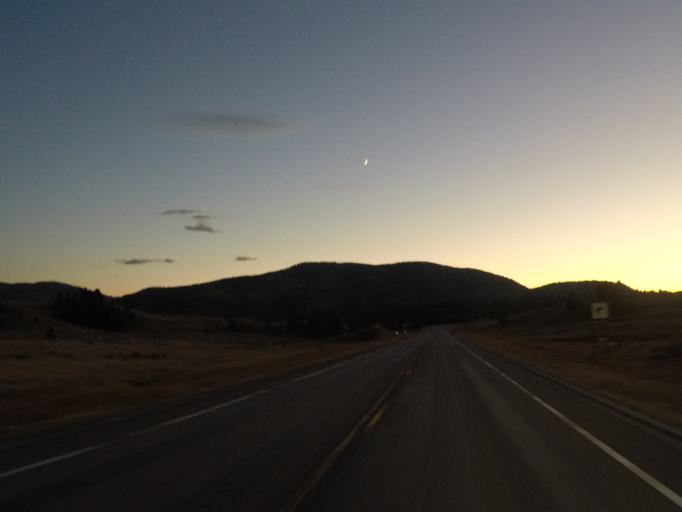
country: US
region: Montana
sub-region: Missoula County
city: Seeley Lake
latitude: 47.0342
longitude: -113.2324
